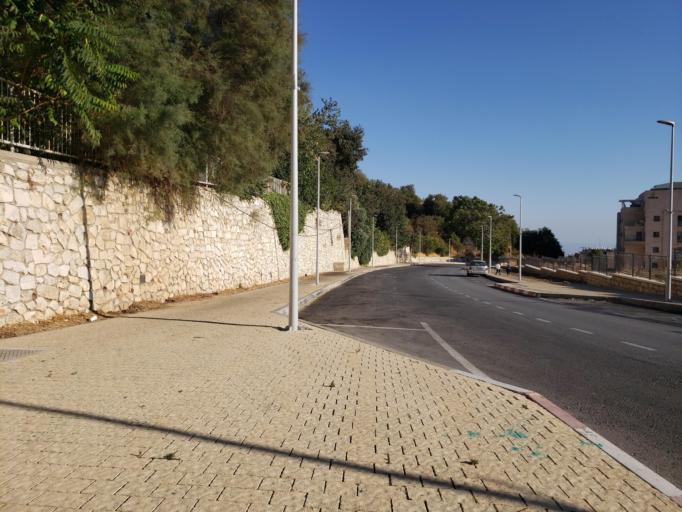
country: IL
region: Northern District
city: Safed
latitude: 32.9639
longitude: 35.4936
